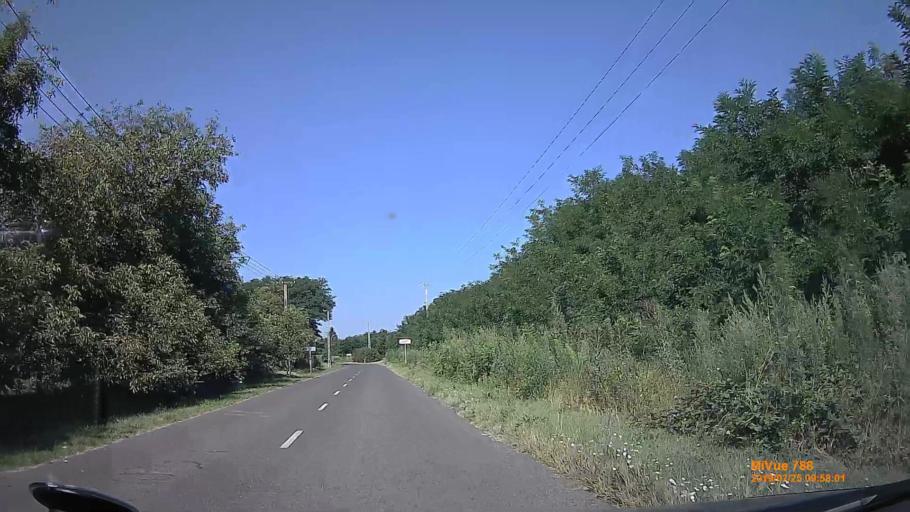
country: HU
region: Szabolcs-Szatmar-Bereg
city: Nyirpazony
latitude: 48.0285
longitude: 21.7849
